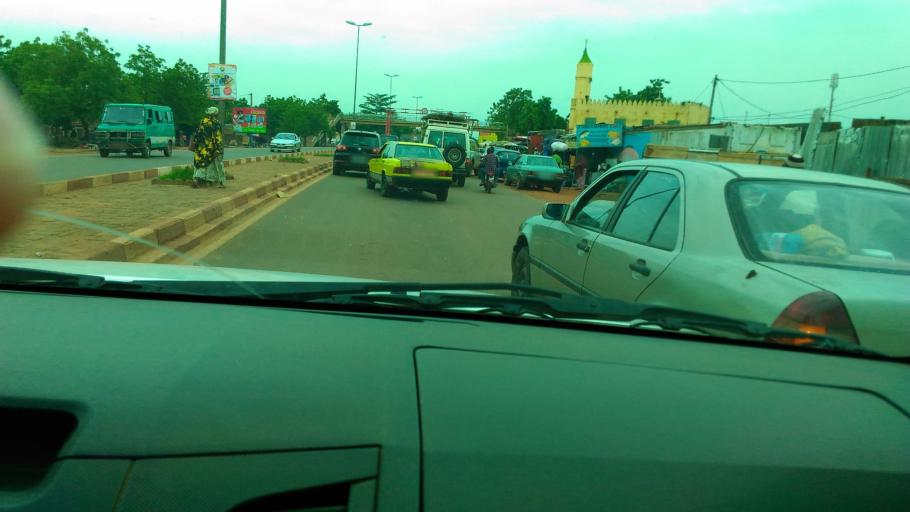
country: ML
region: Bamako
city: Bamako
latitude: 12.5782
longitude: -7.9863
